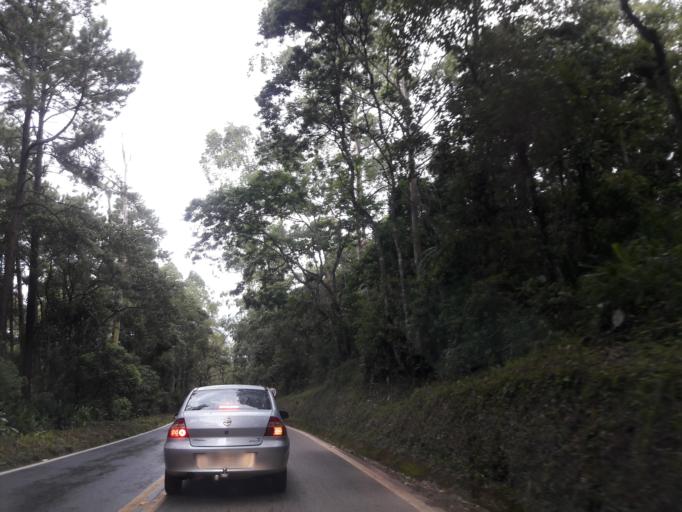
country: BR
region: Sao Paulo
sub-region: Aruja
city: Aruja
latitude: -23.3391
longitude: -46.4341
